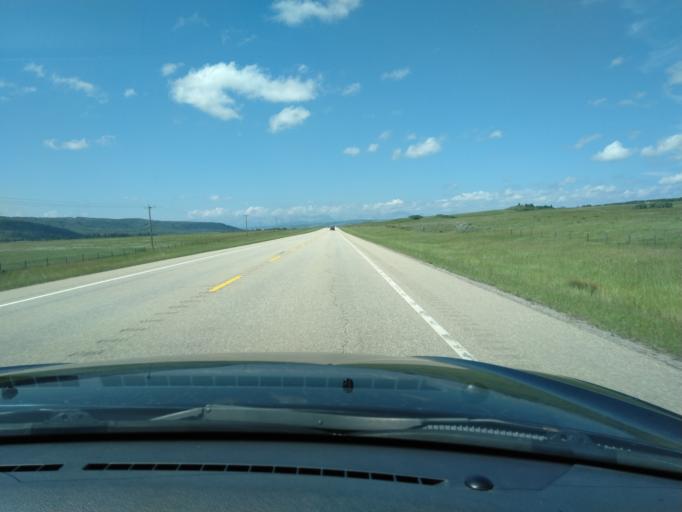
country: CA
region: Alberta
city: Cochrane
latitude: 51.2255
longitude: -114.6112
